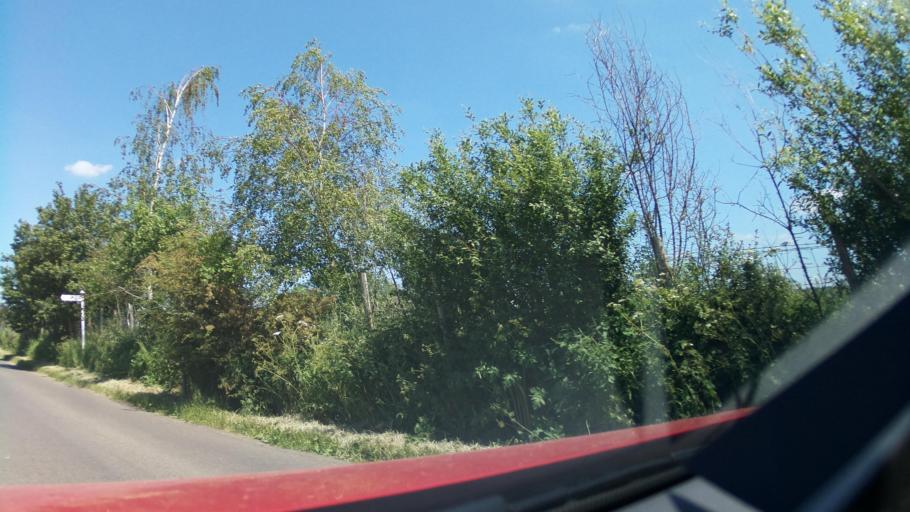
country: GB
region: England
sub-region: Wiltshire
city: Lyneham
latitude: 51.4756
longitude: -1.9540
